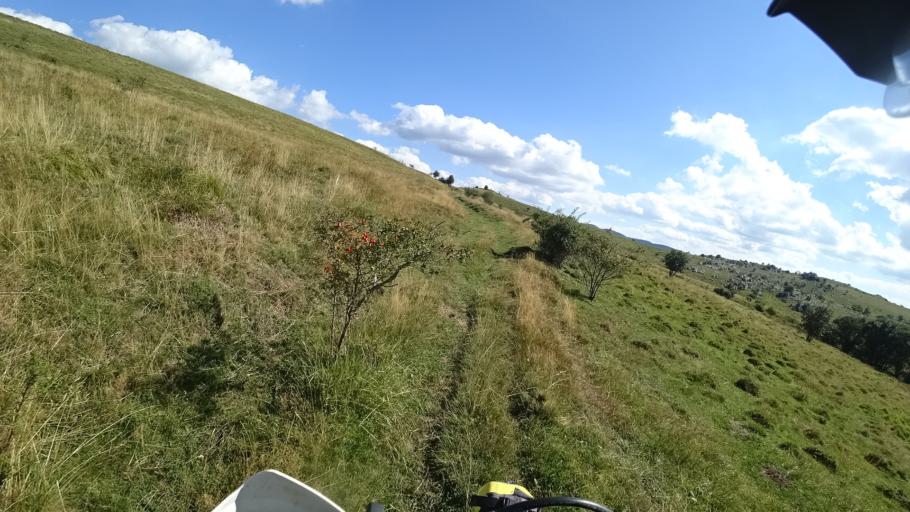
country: HR
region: Zadarska
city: Gracac
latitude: 44.3982
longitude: 16.0109
